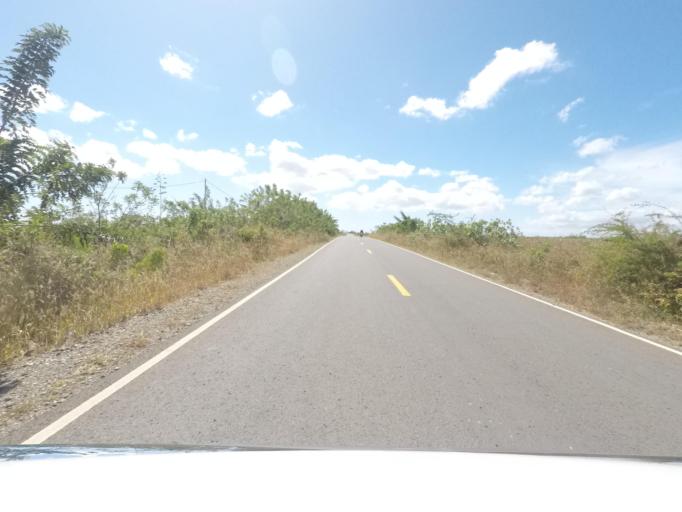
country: TL
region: Baucau
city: Baucau
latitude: -8.4840
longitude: 126.3839
